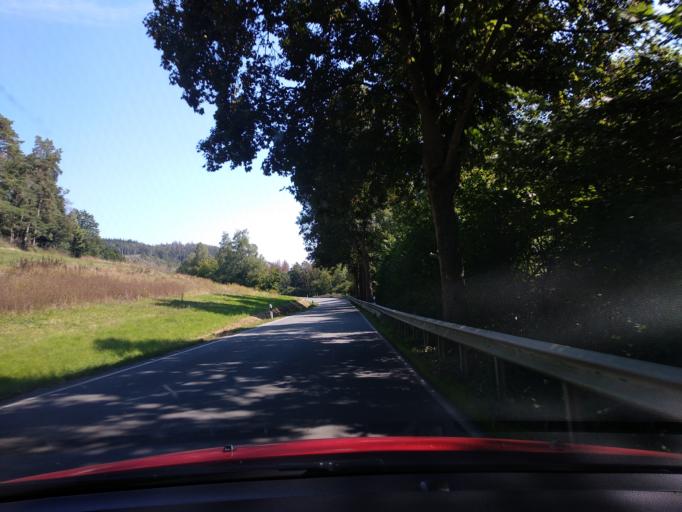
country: DE
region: North Rhine-Westphalia
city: Beverungen
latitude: 51.6810
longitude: 9.3402
